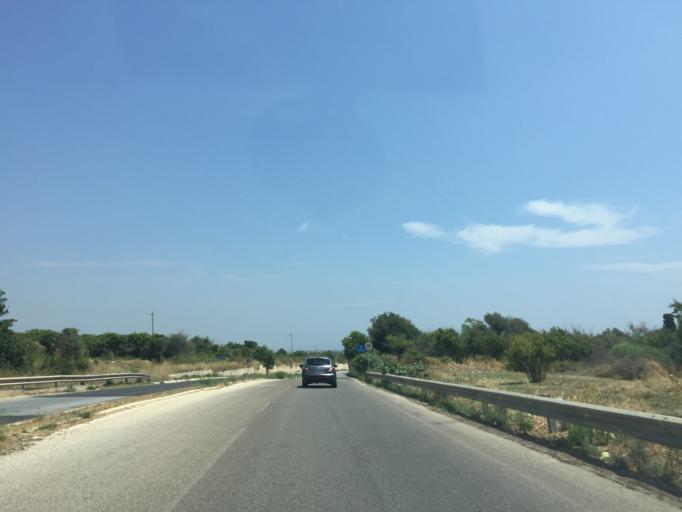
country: IT
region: Sicily
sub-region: Provincia di Siracusa
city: Avola
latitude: 36.9194
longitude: 15.1325
